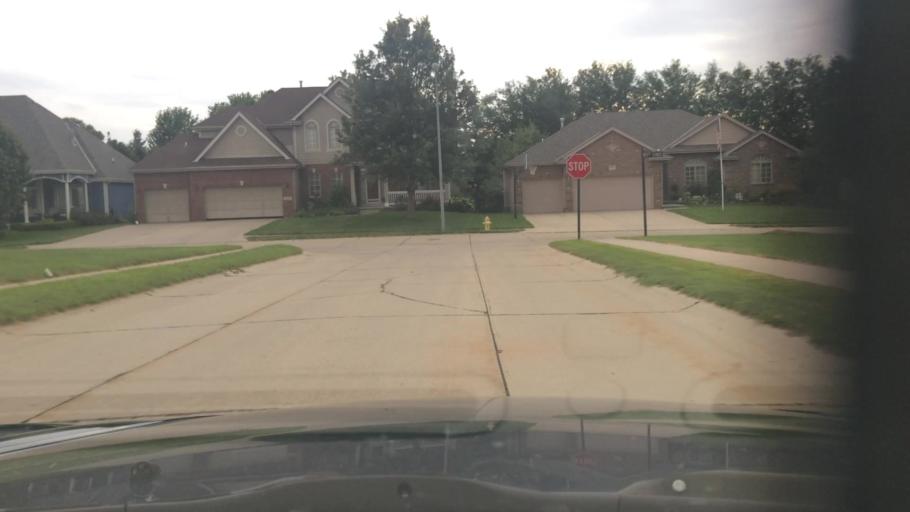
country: US
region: Nebraska
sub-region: Sarpy County
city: La Vista
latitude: 41.1816
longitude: -96.0540
